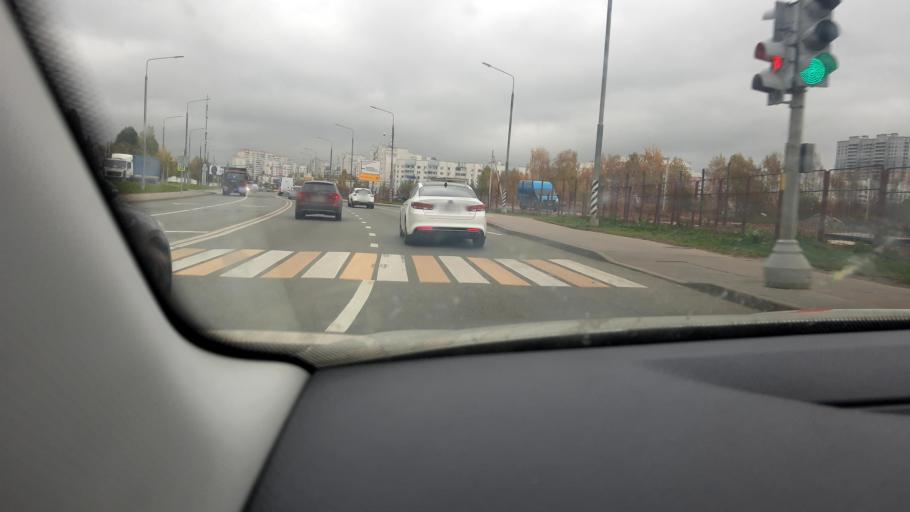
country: RU
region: Moskovskaya
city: Kommunarka
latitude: 55.5399
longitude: 37.4955
